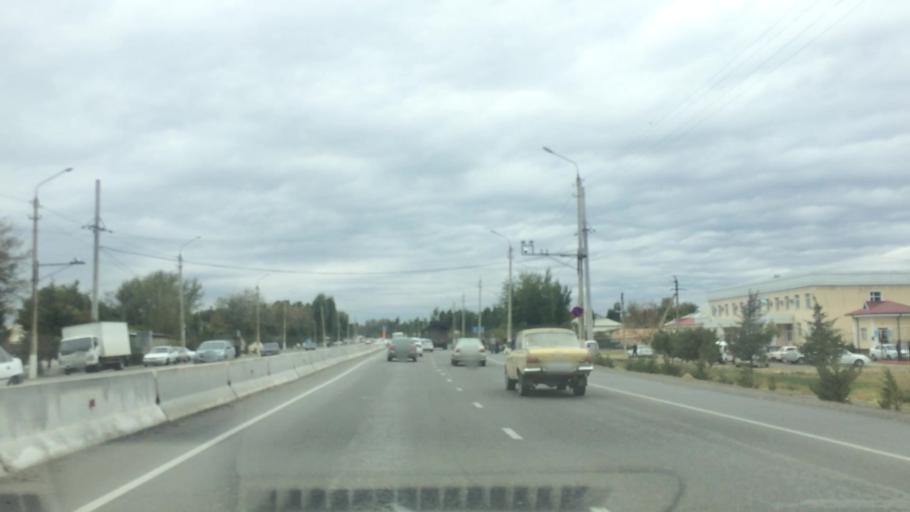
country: UZ
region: Jizzax
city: Jizzax
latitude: 39.9988
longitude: 67.5895
